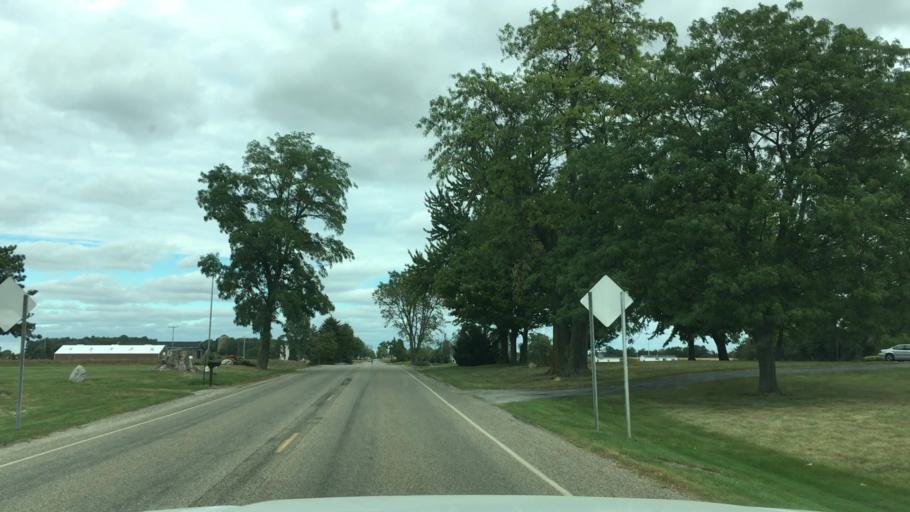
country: US
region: Michigan
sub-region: Ionia County
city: Saranac
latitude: 42.8818
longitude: -85.1341
